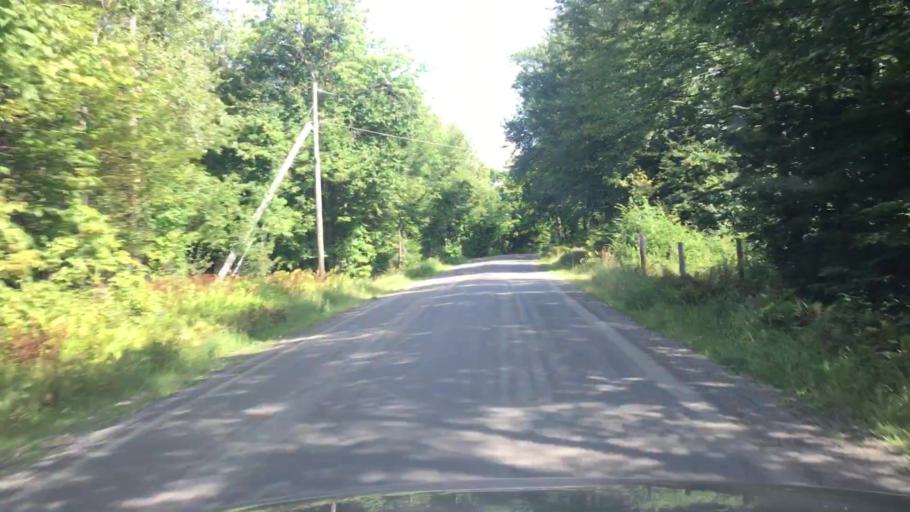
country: US
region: Vermont
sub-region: Windham County
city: Dover
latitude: 42.8372
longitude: -72.8076
